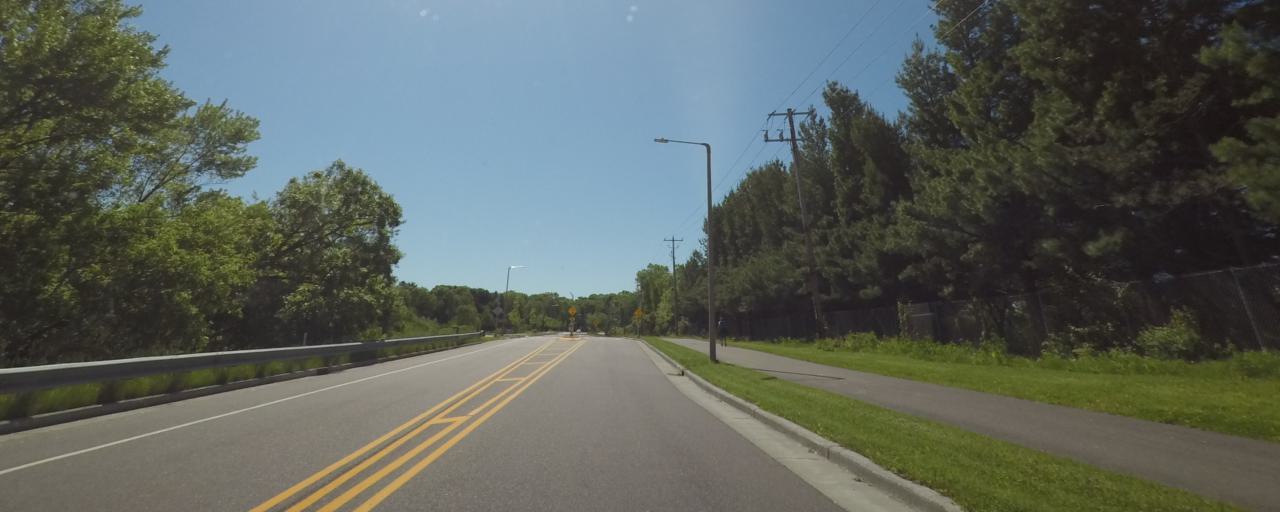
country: US
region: Wisconsin
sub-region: Dane County
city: Verona
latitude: 42.9789
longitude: -89.5322
